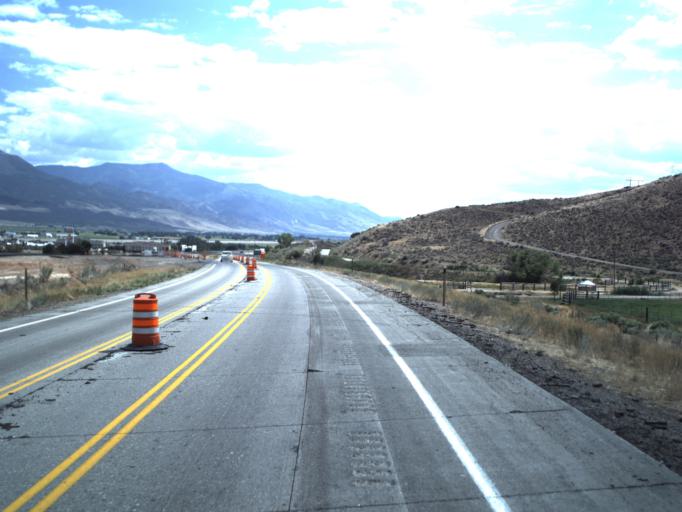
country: US
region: Utah
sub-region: Sevier County
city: Richfield
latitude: 38.7604
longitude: -112.1056
